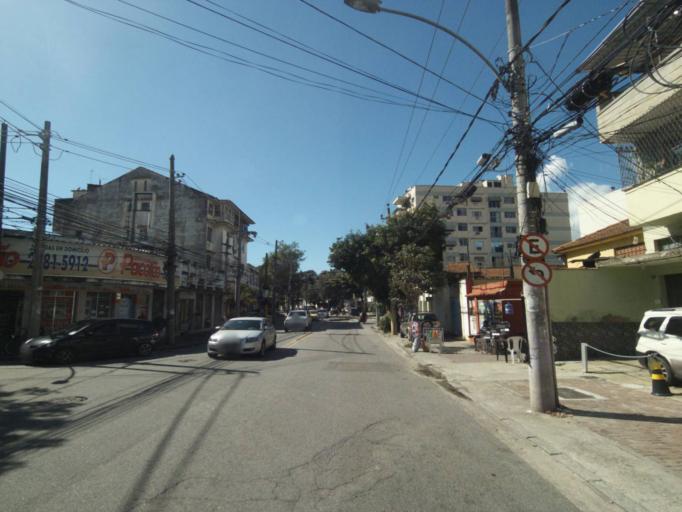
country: BR
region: Rio de Janeiro
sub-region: Rio De Janeiro
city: Rio de Janeiro
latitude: -22.9077
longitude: -43.2777
